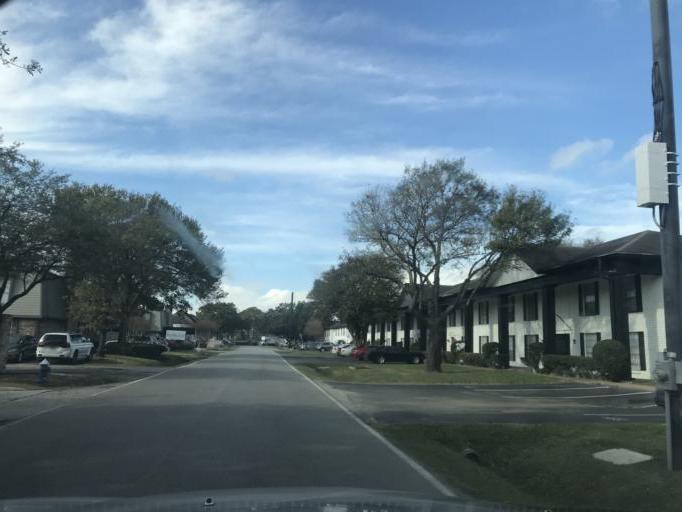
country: US
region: Texas
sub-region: Harris County
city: Hunters Creek Village
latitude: 29.7354
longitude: -95.4875
